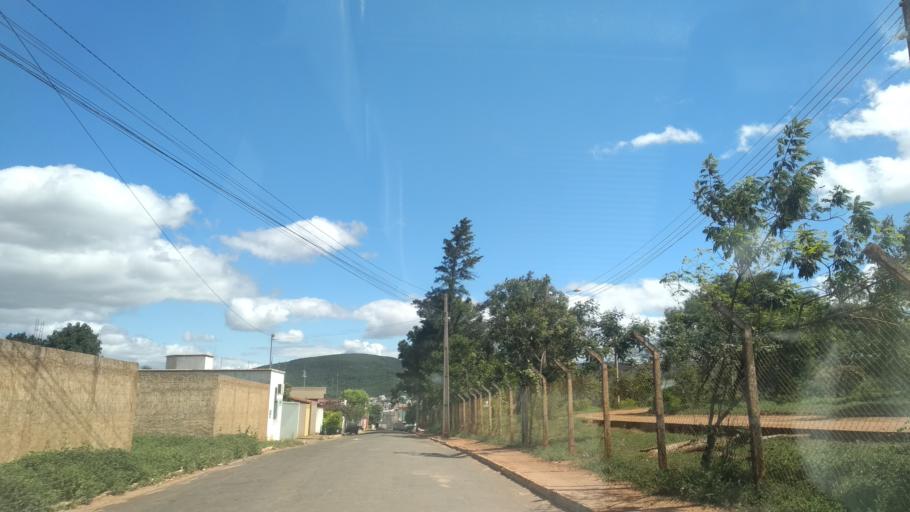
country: BR
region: Bahia
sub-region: Caetite
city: Caetite
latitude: -14.0572
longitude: -42.4866
